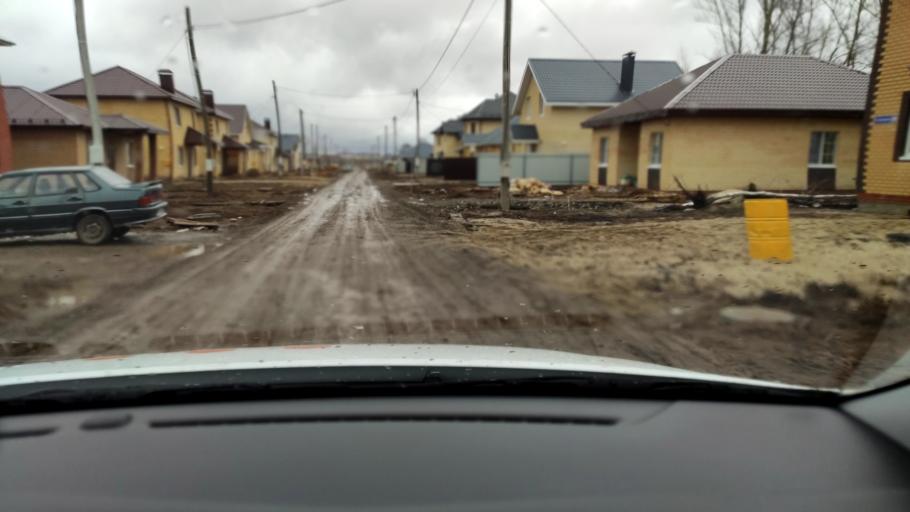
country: RU
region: Tatarstan
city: Stolbishchi
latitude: 55.7196
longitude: 49.3015
